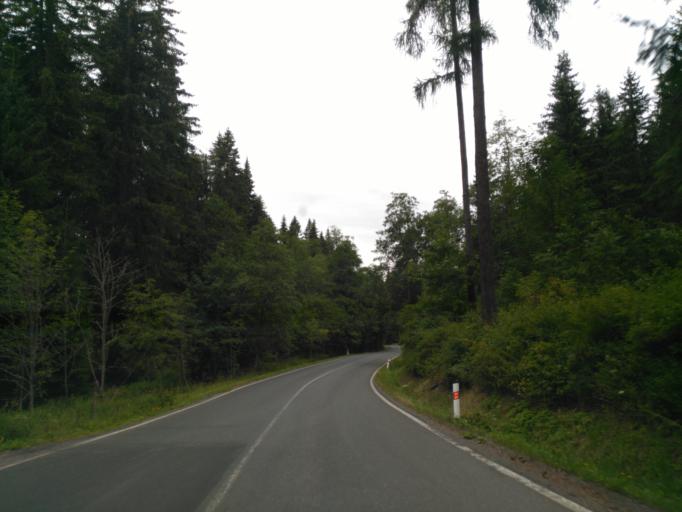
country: DE
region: Saxony
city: Johanngeorgenstadt
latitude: 50.4047
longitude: 12.7409
